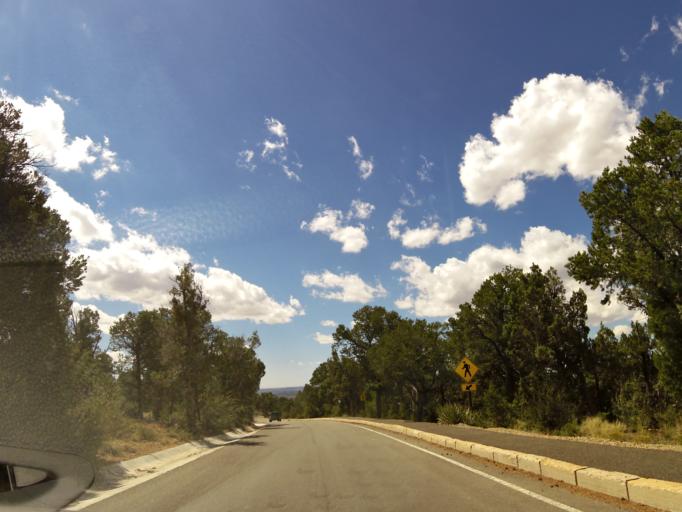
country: US
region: Colorado
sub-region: Montezuma County
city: Cortez
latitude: 37.1858
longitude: -108.4899
